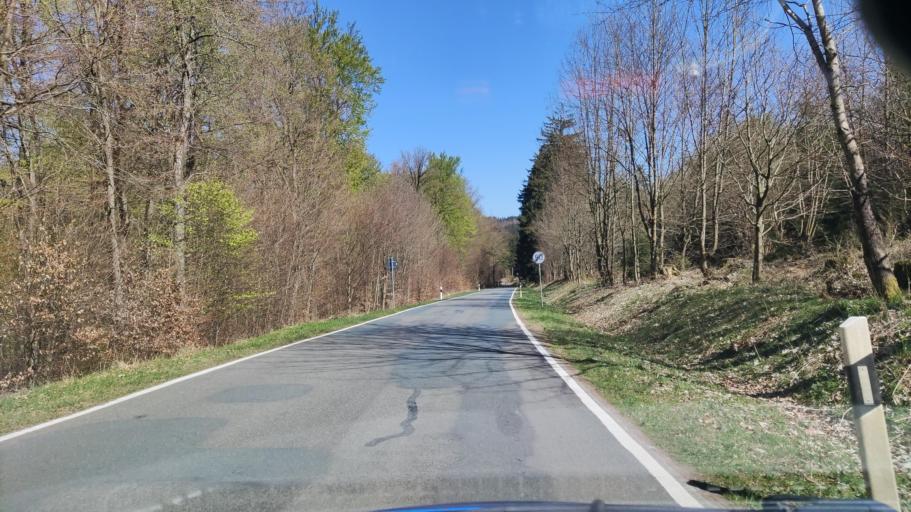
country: DE
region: Lower Saxony
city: Eimen
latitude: 51.8947
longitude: 9.8095
